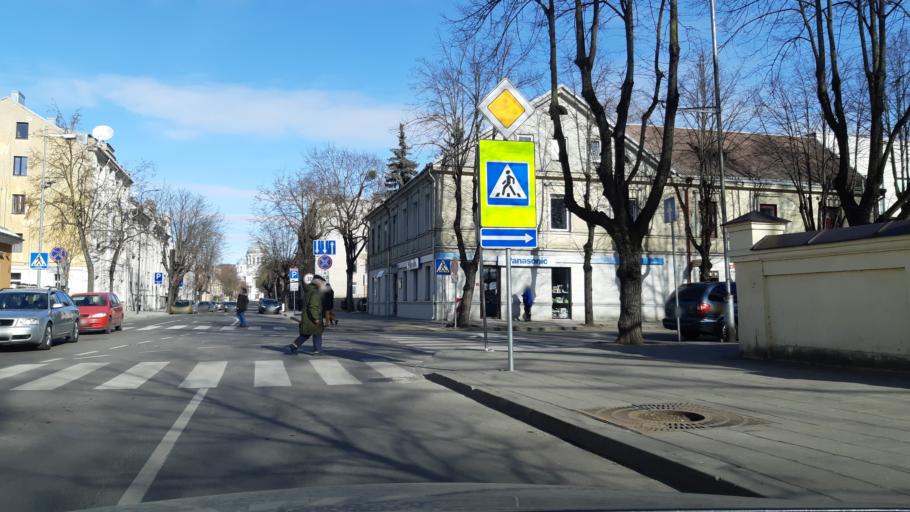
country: LT
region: Kauno apskritis
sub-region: Kaunas
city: Kaunas
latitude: 54.8918
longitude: 23.9209
